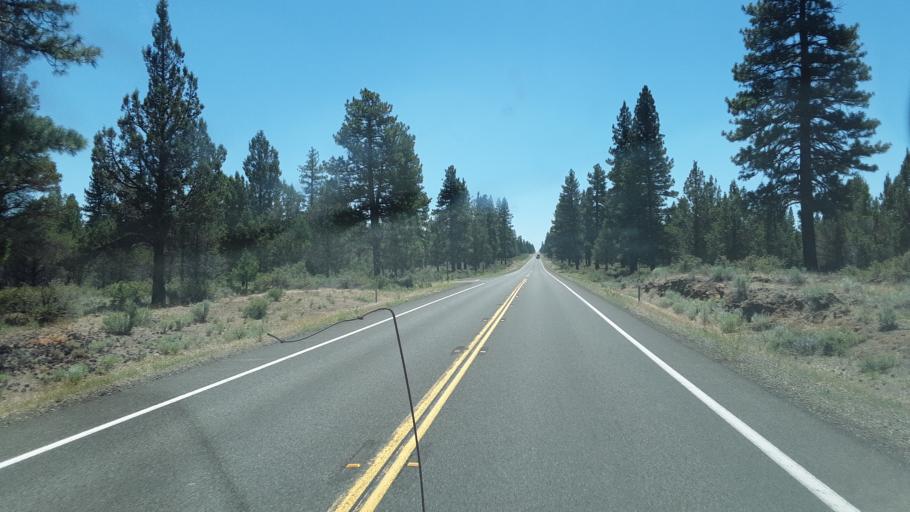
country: US
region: California
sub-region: Siskiyou County
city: Tulelake
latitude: 41.6277
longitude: -121.2249
